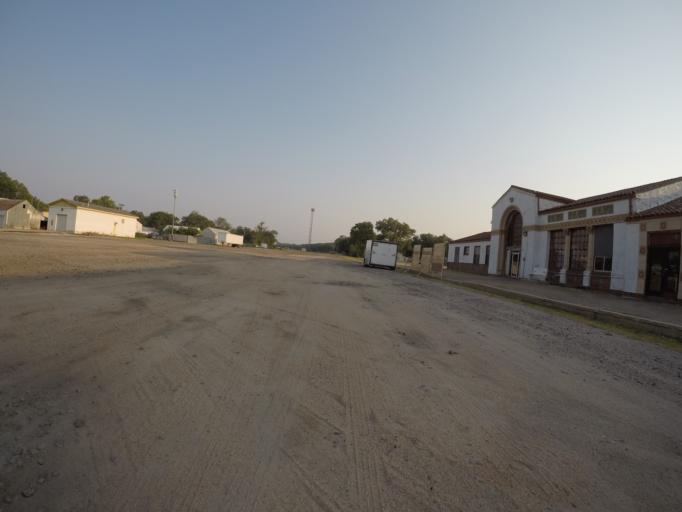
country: US
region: Kansas
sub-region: Marshall County
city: Marysville
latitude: 39.8440
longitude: -96.6493
